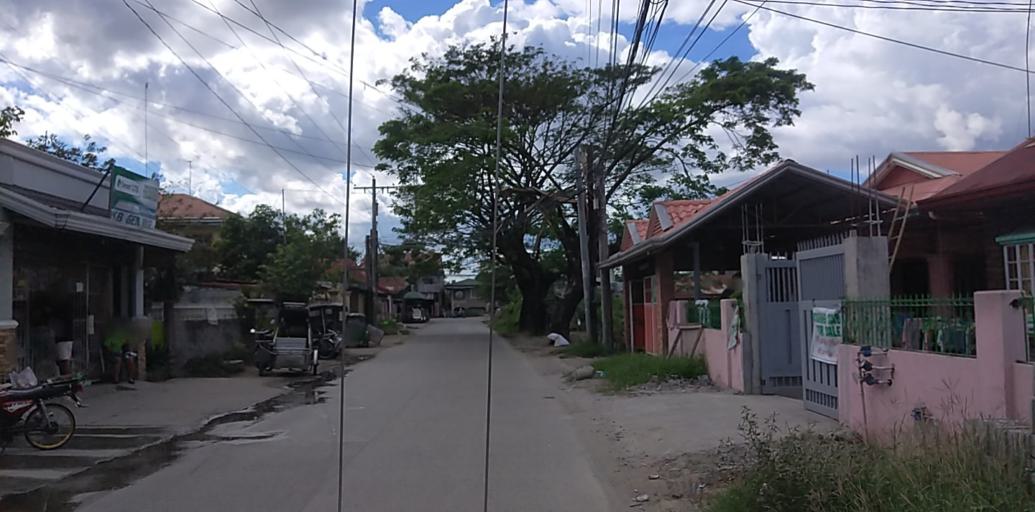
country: PH
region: Central Luzon
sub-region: Province of Pampanga
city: Arayat
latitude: 15.1399
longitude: 120.7739
